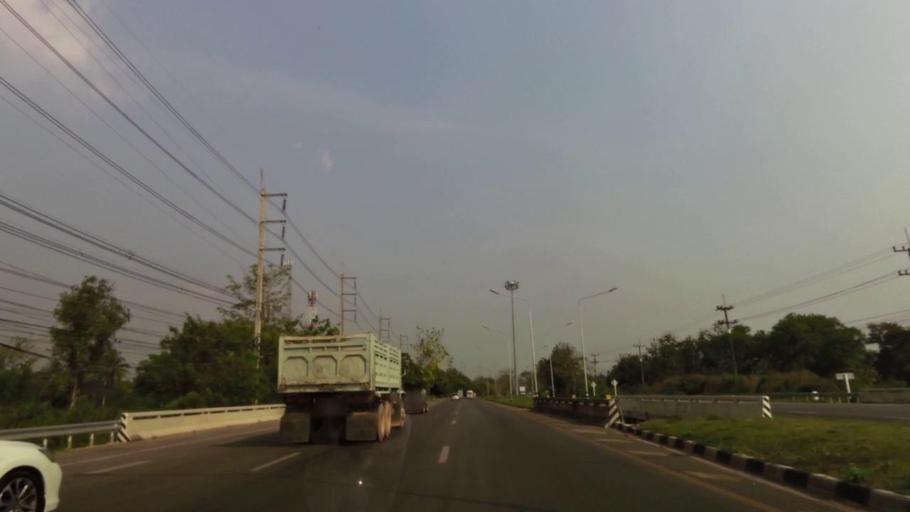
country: TH
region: Rayong
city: Klaeng
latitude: 12.7857
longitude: 101.6793
